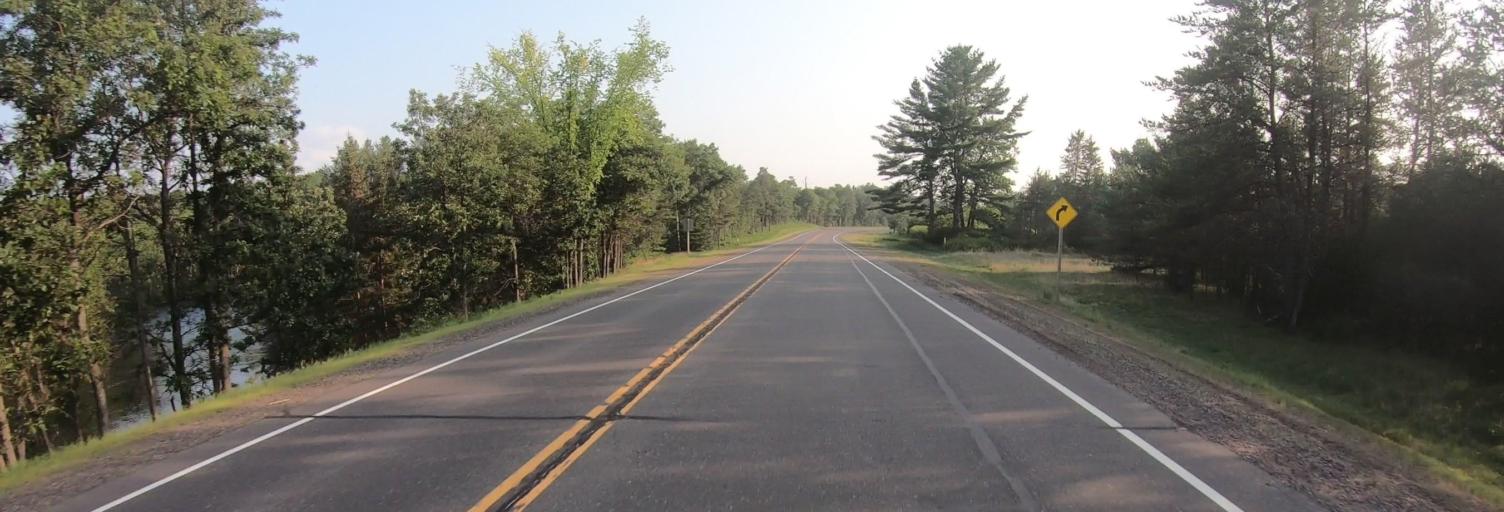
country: US
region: Wisconsin
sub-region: Sawyer County
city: Hayward
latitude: 45.9674
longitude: -91.6674
